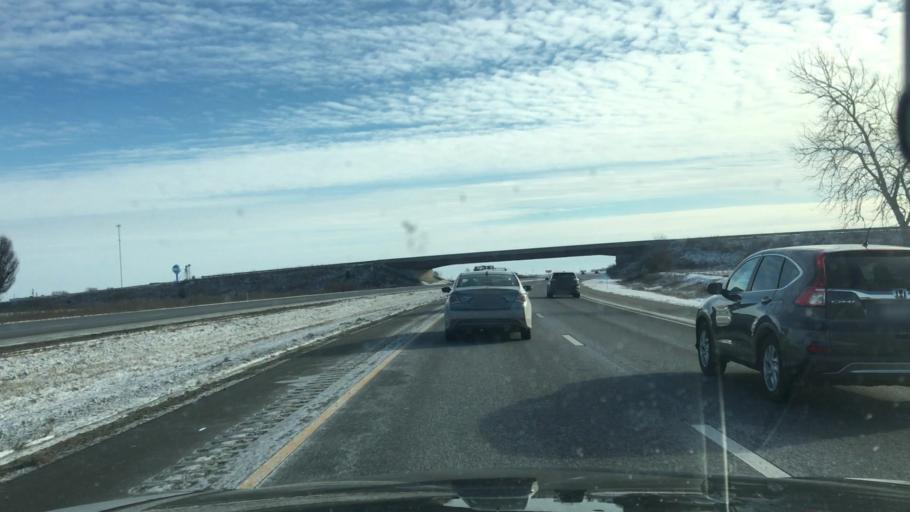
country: US
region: Illinois
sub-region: Marshall County
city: Wenona
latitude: 41.0445
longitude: -89.0576
